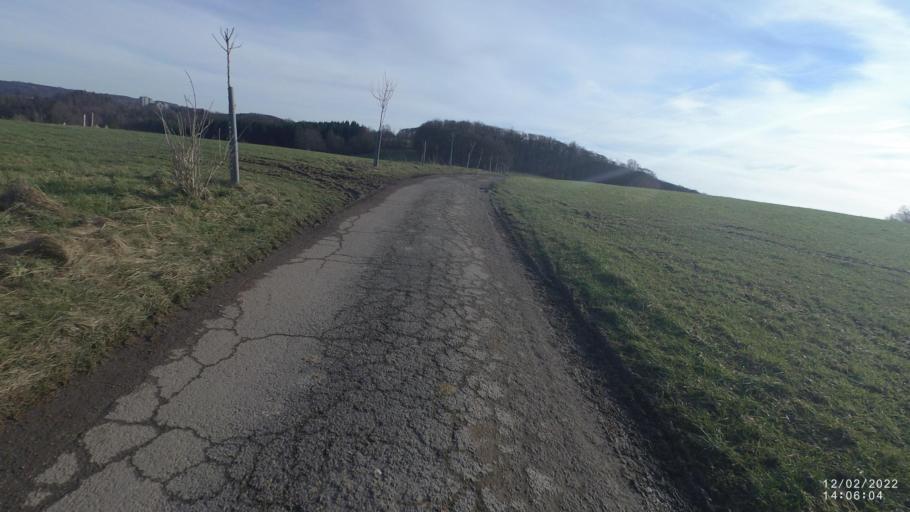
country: DE
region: North Rhine-Westphalia
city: Altena
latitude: 51.2950
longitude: 7.6962
